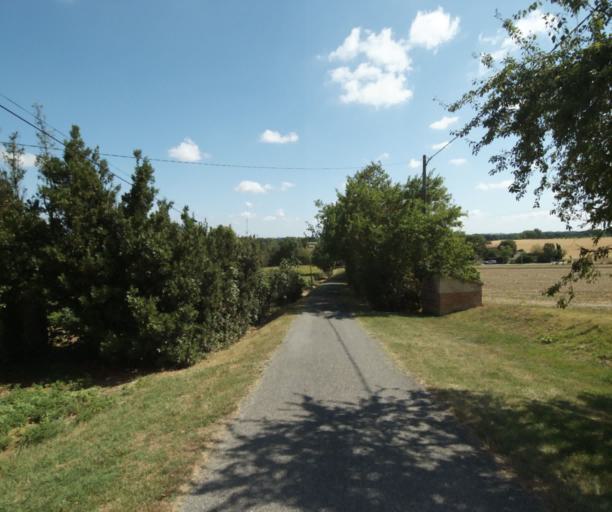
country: FR
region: Midi-Pyrenees
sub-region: Departement de la Haute-Garonne
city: Auriac-sur-Vendinelle
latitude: 43.4656
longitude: 1.7956
